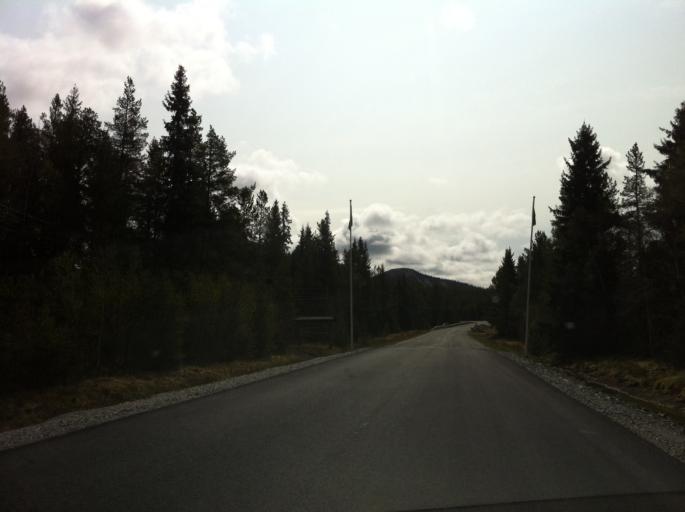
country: NO
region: Hedmark
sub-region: Engerdal
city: Engerdal
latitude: 62.4395
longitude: 12.6810
